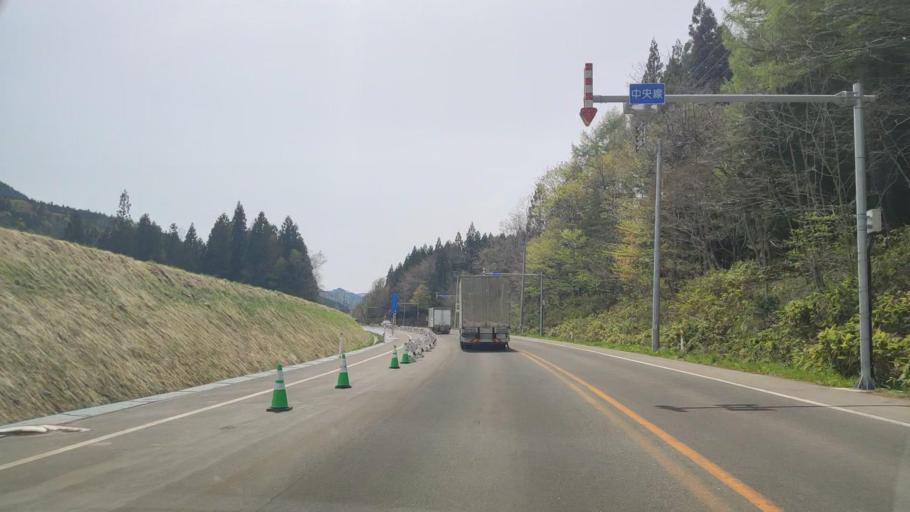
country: JP
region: Aomori
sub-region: Misawa Shi
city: Inuotose
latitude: 40.7866
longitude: 141.0704
